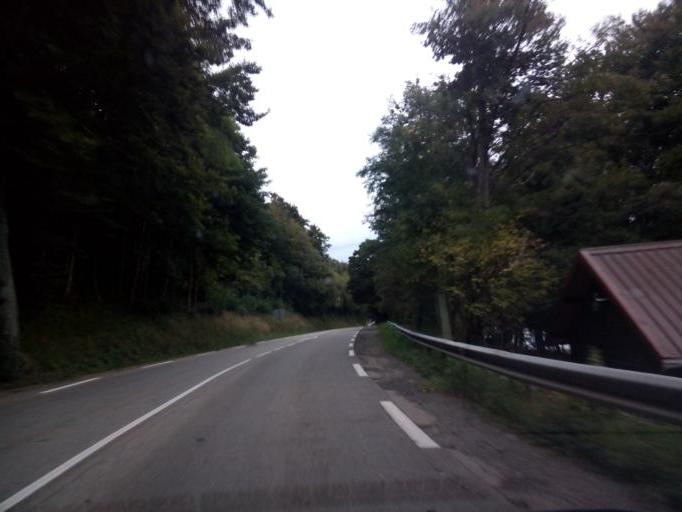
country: FR
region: Rhone-Alpes
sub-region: Departement de l'Isere
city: Pierre-Chatel
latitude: 45.0012
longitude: 5.7719
